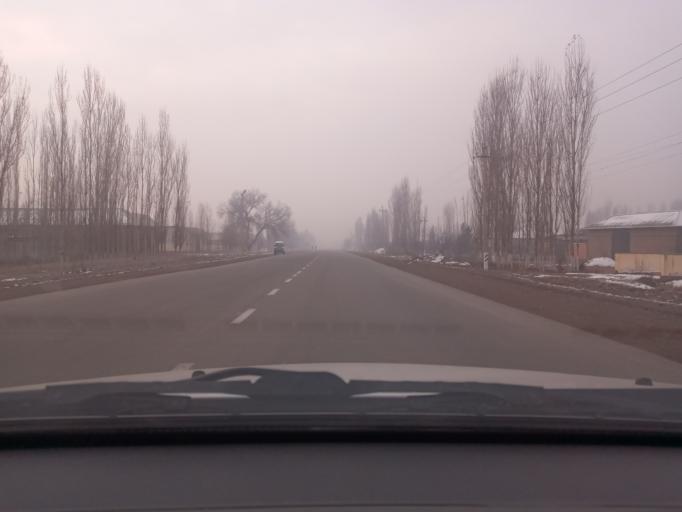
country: UZ
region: Namangan
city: Pop
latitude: 40.8897
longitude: 71.1472
